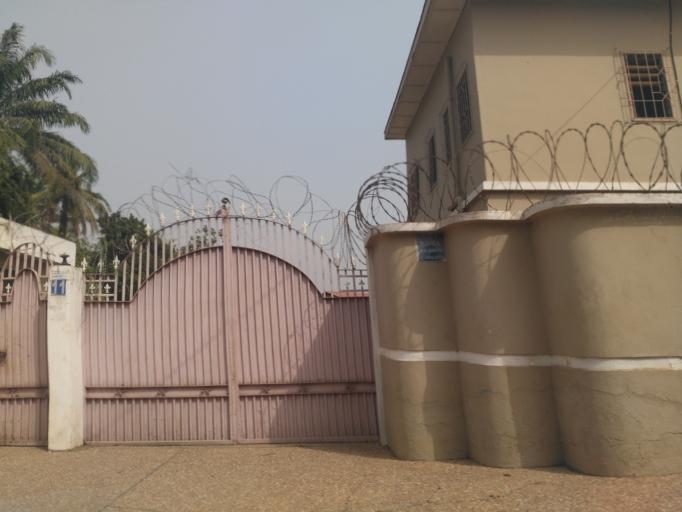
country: GH
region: Ashanti
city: Kumasi
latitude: 6.6769
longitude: -1.6031
